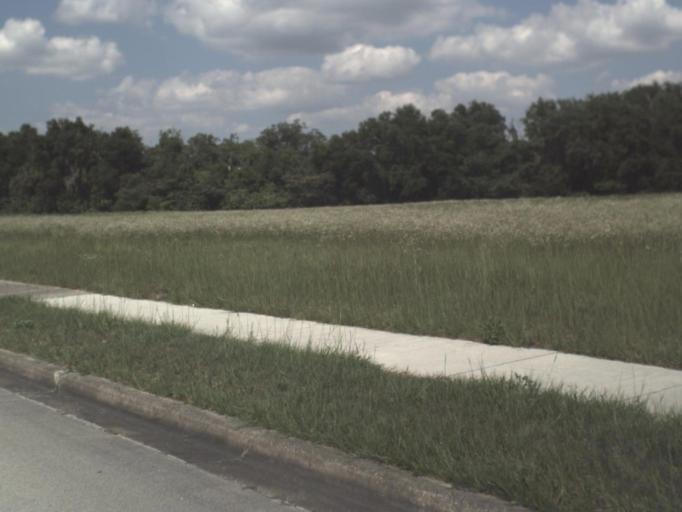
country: US
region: Florida
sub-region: Alachua County
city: Hawthorne
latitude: 29.5843
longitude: -82.0855
